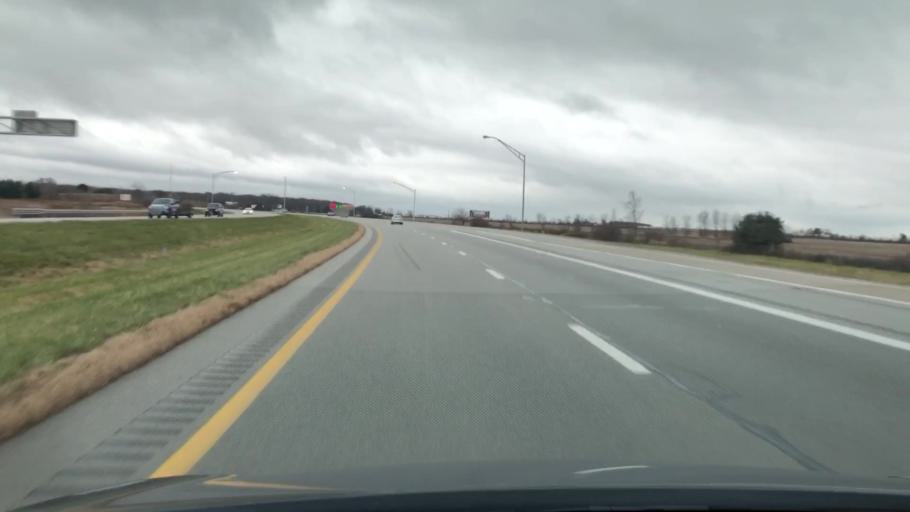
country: US
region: Ohio
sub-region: Wood County
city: Walbridge
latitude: 41.5848
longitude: -83.4768
